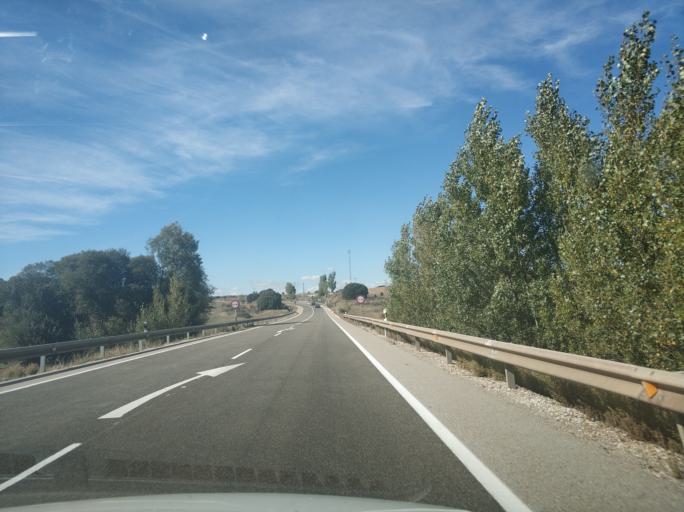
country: ES
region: Castille and Leon
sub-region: Provincia de Burgos
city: Cubillo del Campo
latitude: 42.1740
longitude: -3.6186
